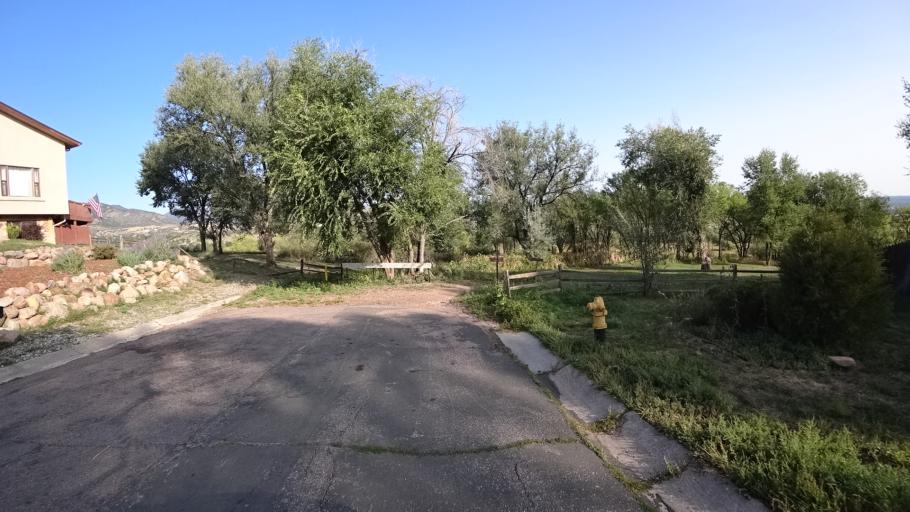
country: US
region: Colorado
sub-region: El Paso County
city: Colorado Springs
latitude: 38.8173
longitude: -104.8537
